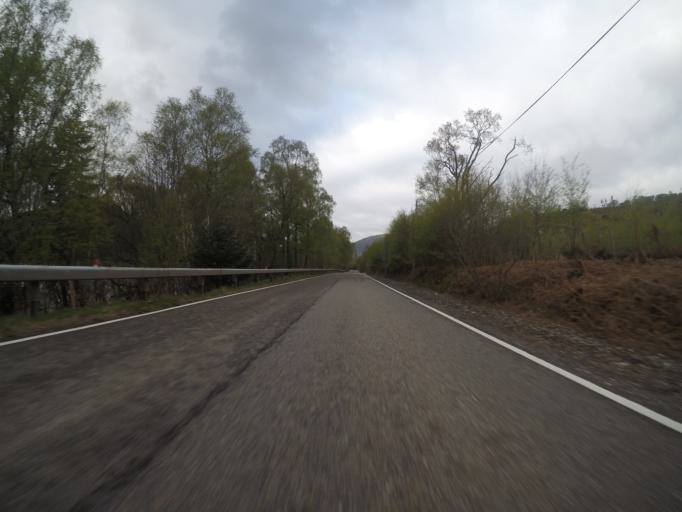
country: GB
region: Scotland
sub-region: Highland
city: Kingussie
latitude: 56.9587
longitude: -4.4663
